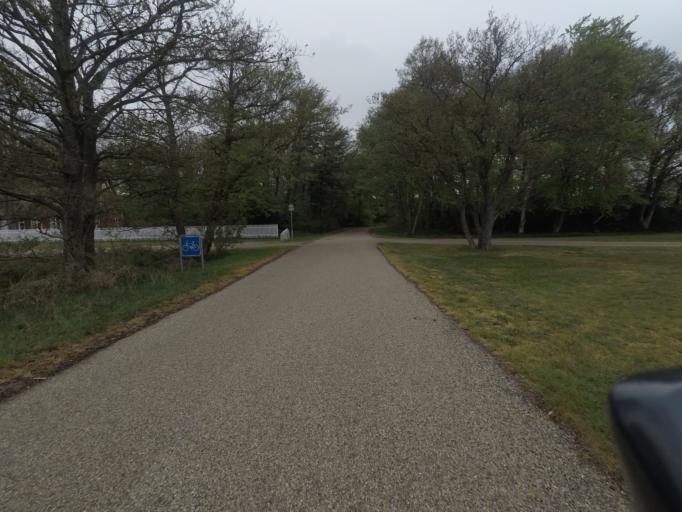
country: DE
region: Schleswig-Holstein
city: List
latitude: 55.1124
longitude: 8.5415
